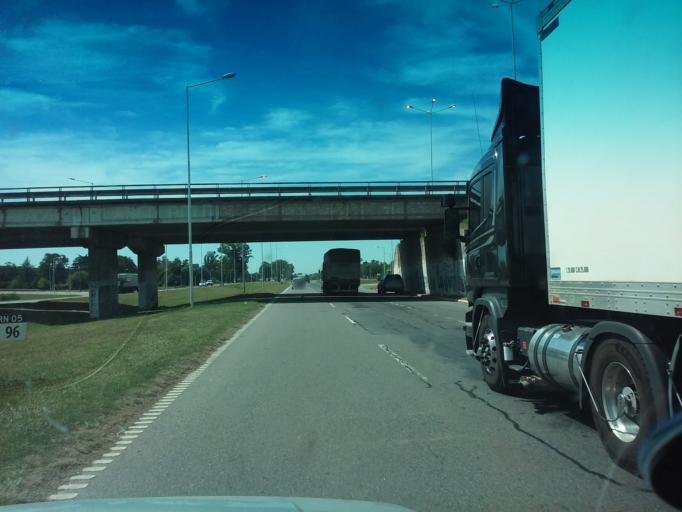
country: AR
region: Buenos Aires
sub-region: Partido de Mercedes
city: Mercedes
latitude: -34.6650
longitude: -59.4005
